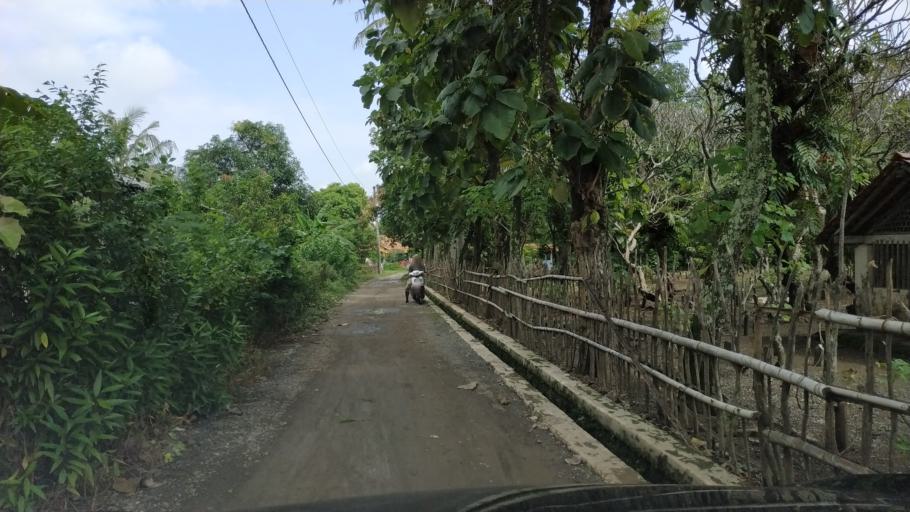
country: ID
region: Central Java
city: Margasari
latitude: -7.0928
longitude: 108.9767
